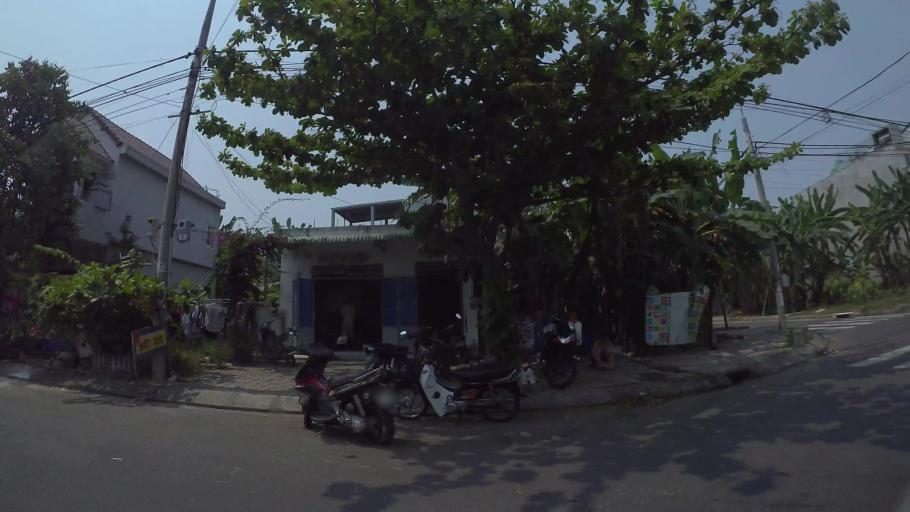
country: VN
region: Da Nang
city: Cam Le
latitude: 16.0010
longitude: 108.2194
